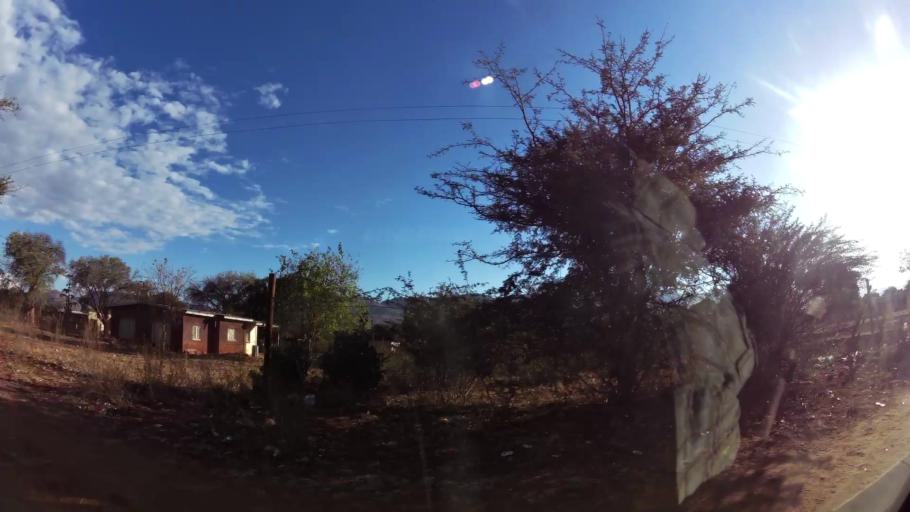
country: ZA
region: Limpopo
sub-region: Waterberg District Municipality
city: Mokopane
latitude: -24.1685
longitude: 28.9742
